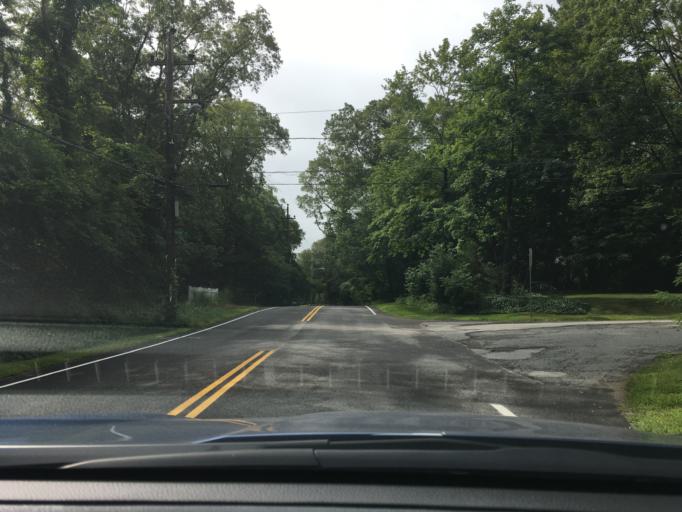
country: US
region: Rhode Island
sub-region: Kent County
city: East Greenwich
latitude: 41.6517
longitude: -71.4747
